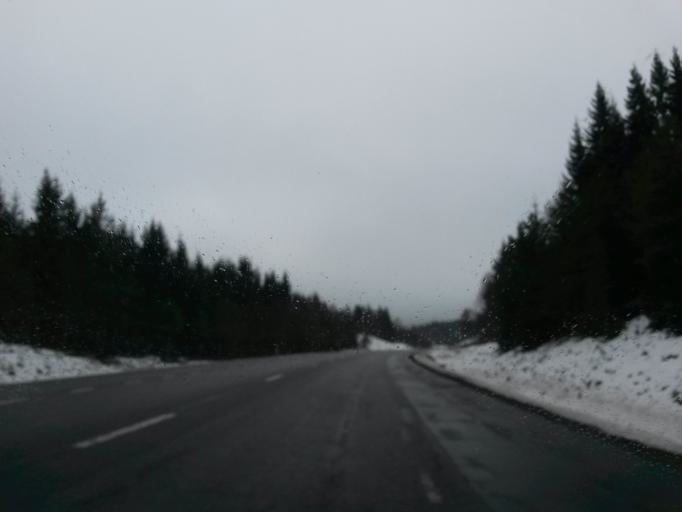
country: SE
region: Vaestra Goetaland
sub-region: Boras Kommun
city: Viskafors
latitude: 57.6051
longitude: 12.8735
